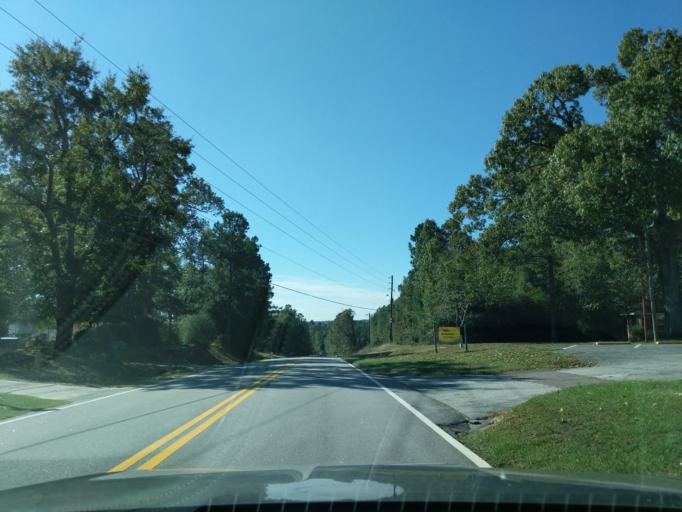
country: US
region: Georgia
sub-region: Richmond County
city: Hephzibah
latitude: 33.3219
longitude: -82.0161
